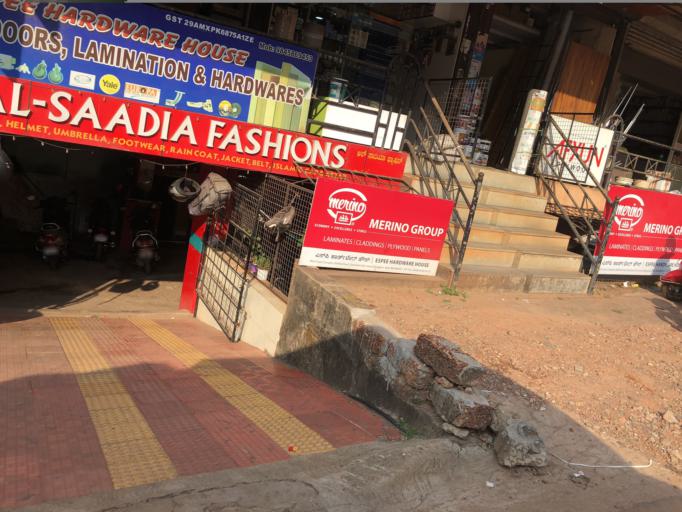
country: IN
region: Karnataka
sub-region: Dakshina Kannada
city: Mangalore
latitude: 12.8631
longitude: 74.8354
